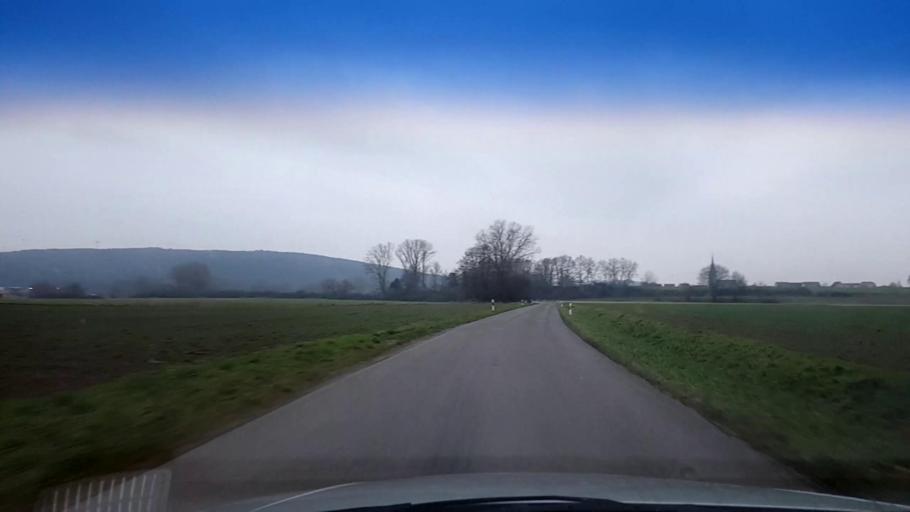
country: DE
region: Bavaria
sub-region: Upper Franconia
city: Rattelsdorf
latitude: 50.0179
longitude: 10.9091
